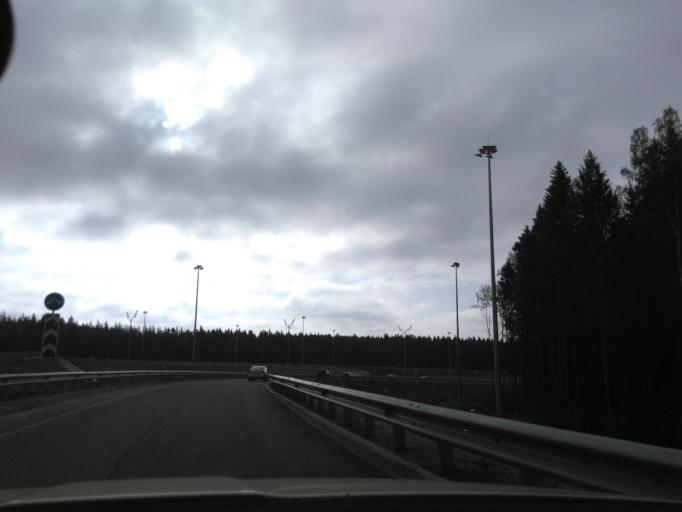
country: RU
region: Moskovskaya
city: Rzhavki
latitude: 56.0073
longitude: 37.2845
